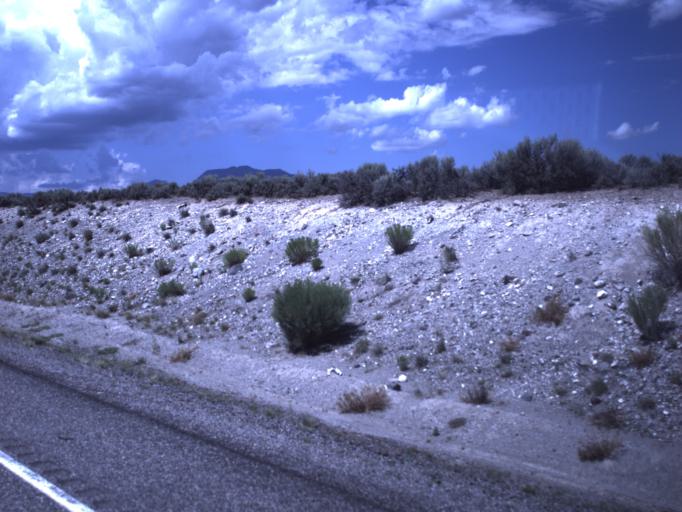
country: US
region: Utah
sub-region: Garfield County
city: Panguitch
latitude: 37.9815
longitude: -112.4003
